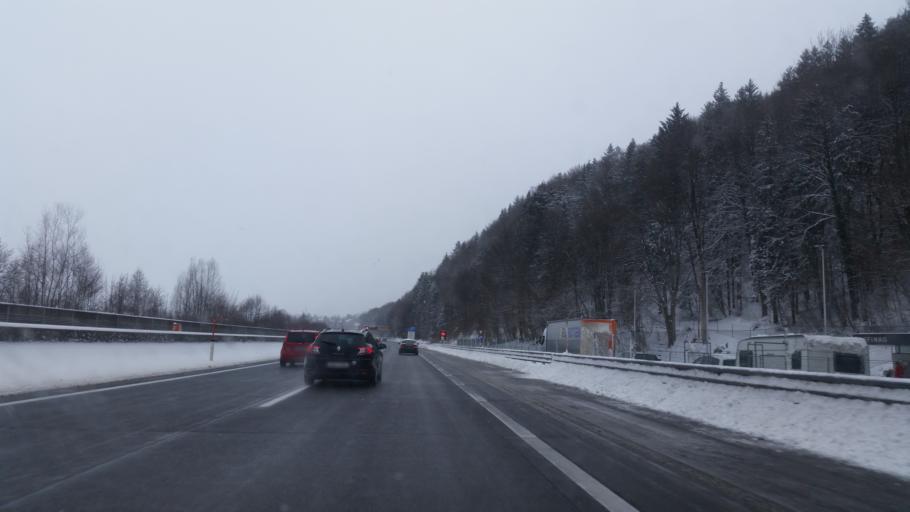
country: AT
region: Salzburg
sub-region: Politischer Bezirk Hallein
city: Adnet
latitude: 47.6784
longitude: 13.1232
